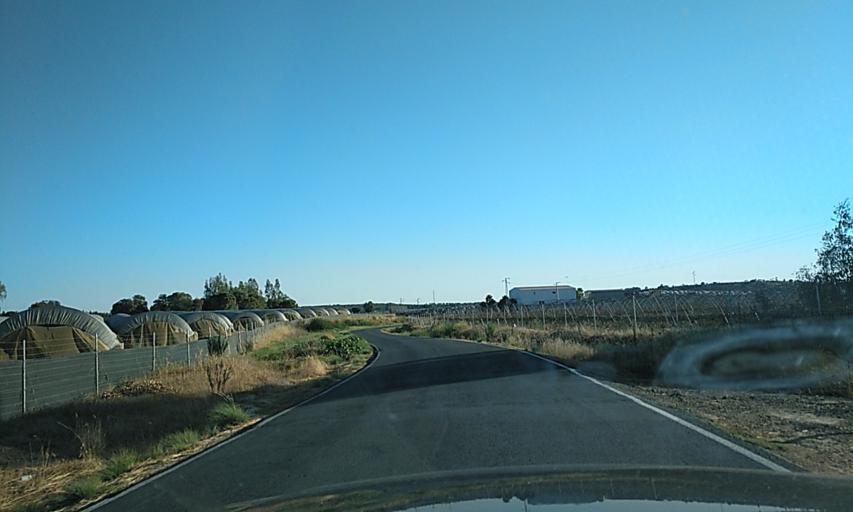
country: ES
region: Andalusia
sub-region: Provincia de Huelva
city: San Bartolome de la Torre
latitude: 37.4207
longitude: -7.1104
